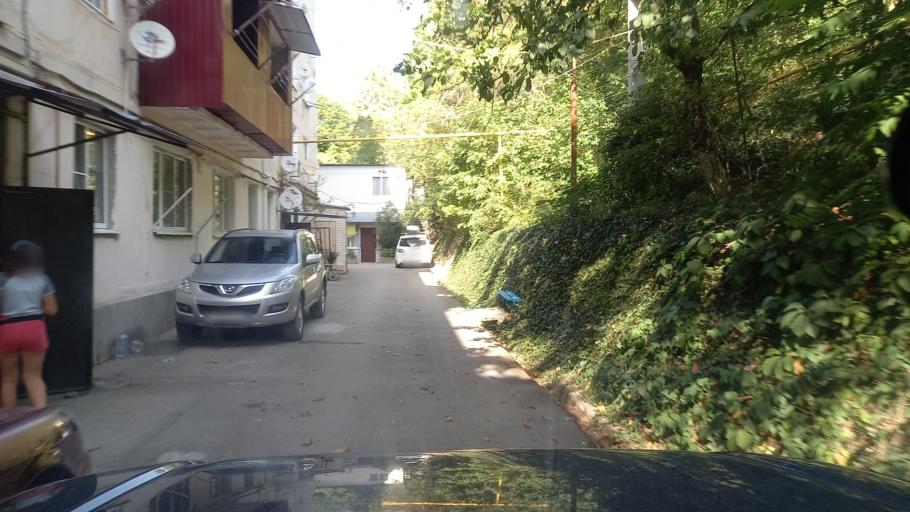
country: RU
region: Krasnodarskiy
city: Pshada
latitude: 44.3765
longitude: 38.4018
